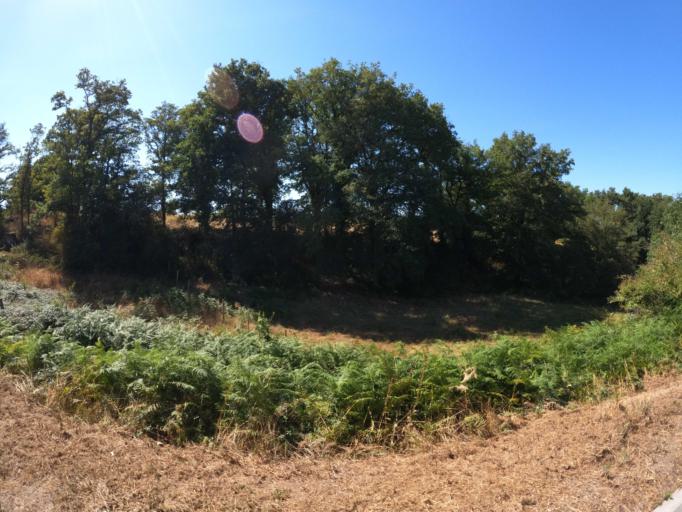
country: FR
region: Pays de la Loire
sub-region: Departement de la Vendee
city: Les Landes-Genusson
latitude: 46.9696
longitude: -1.0951
